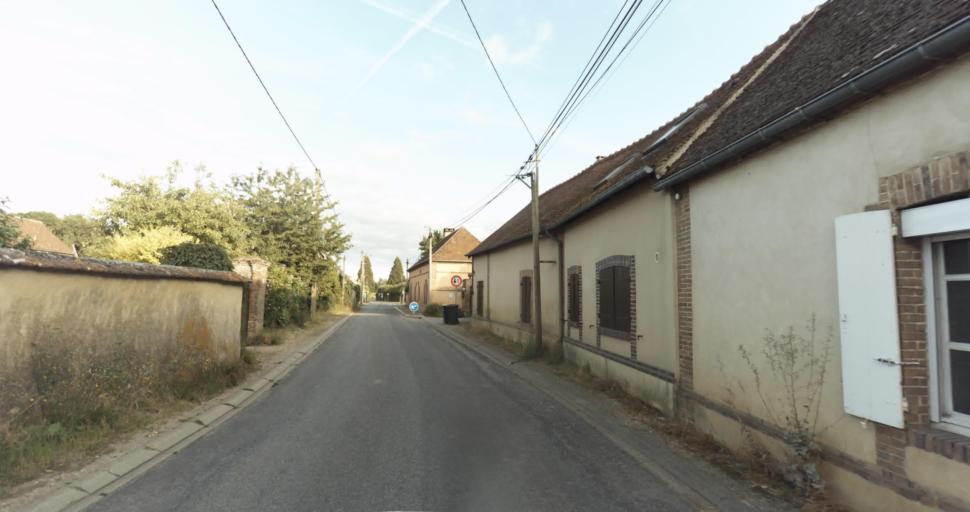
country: FR
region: Haute-Normandie
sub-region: Departement de l'Eure
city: Marcilly-sur-Eure
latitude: 48.8466
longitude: 1.2756
